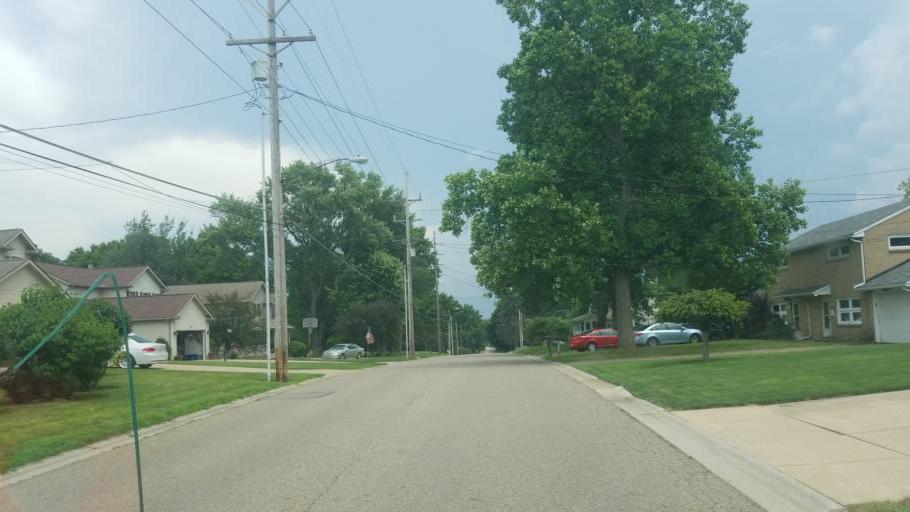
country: US
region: Ohio
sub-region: Stark County
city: North Canton
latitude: 40.8828
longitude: -81.3920
